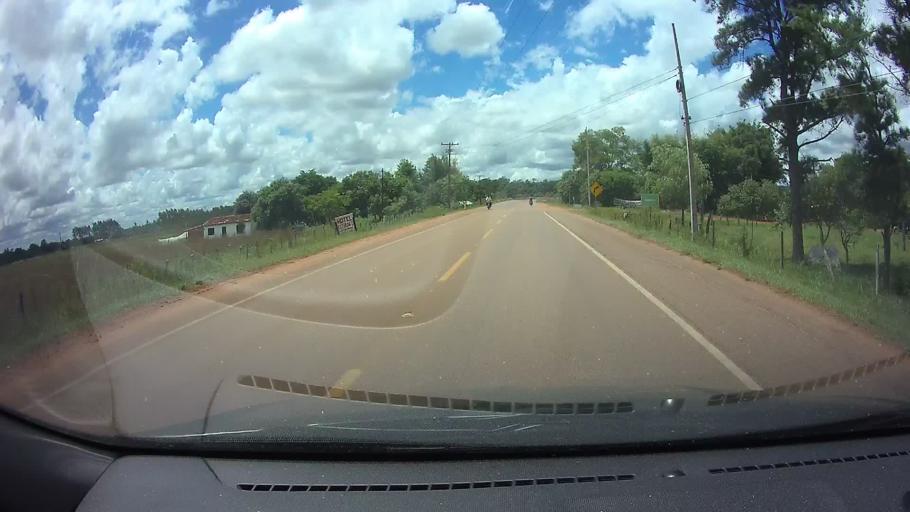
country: PY
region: Paraguari
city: La Colmena
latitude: -25.8982
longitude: -56.7934
